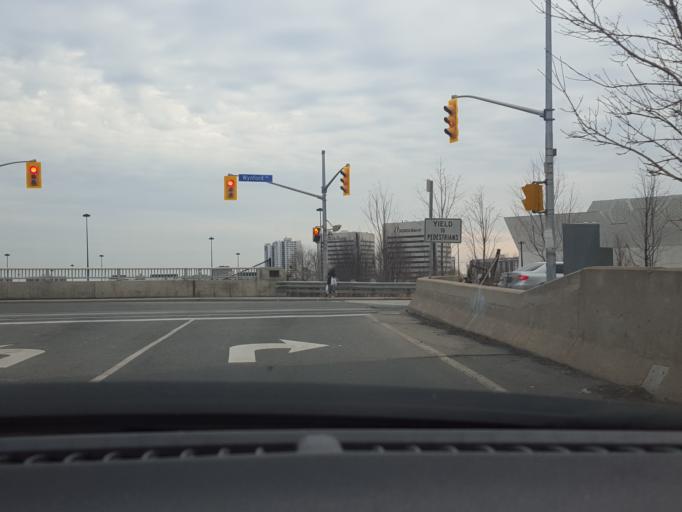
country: CA
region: Ontario
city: Willowdale
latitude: 43.7270
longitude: -79.3310
